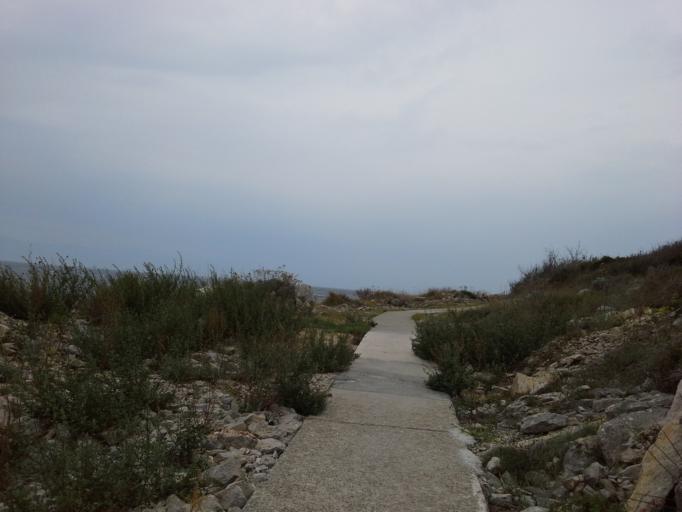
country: HR
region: Primorsko-Goranska
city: Mali Losinj
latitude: 44.5414
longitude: 14.4672
